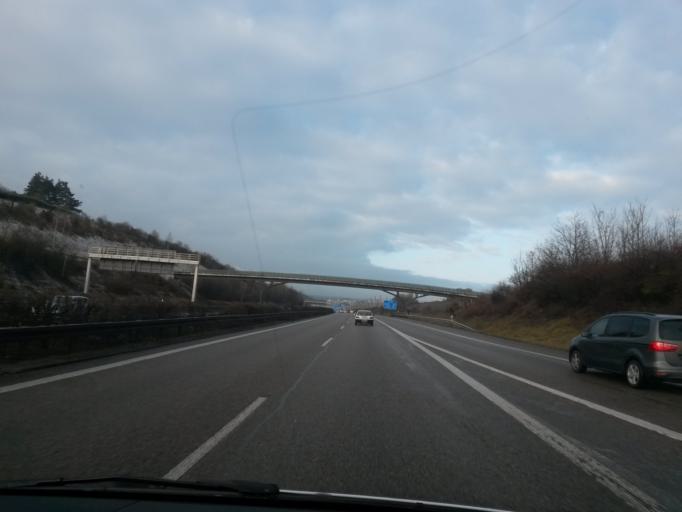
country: DE
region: Baden-Wuerttemberg
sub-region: Regierungsbezirk Stuttgart
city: Leonberg
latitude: 48.7832
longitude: 9.0065
